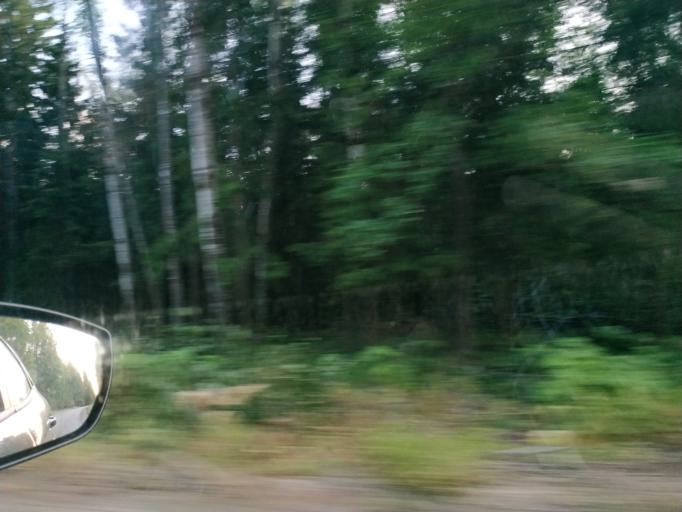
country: RU
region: Moskovskaya
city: Krasnoarmeysk
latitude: 56.0750
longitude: 38.2465
